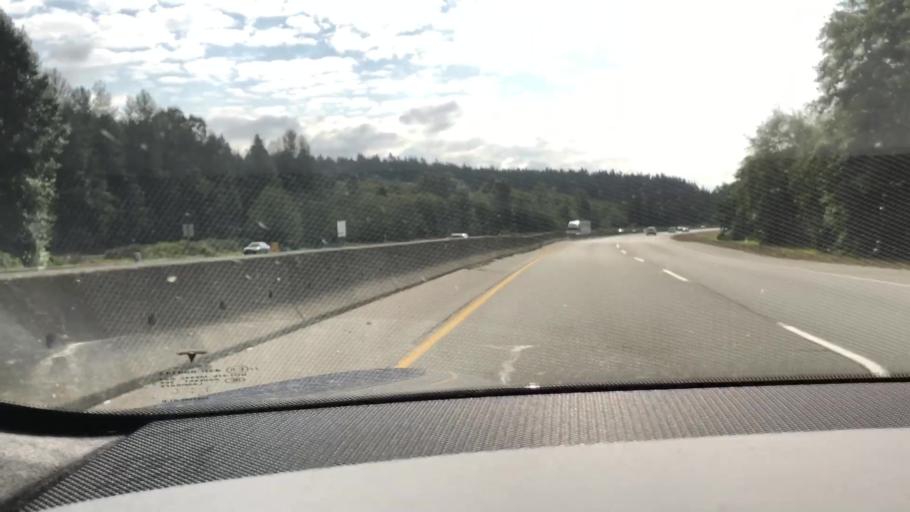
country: CA
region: British Columbia
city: Delta
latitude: 49.1131
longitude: -122.9105
